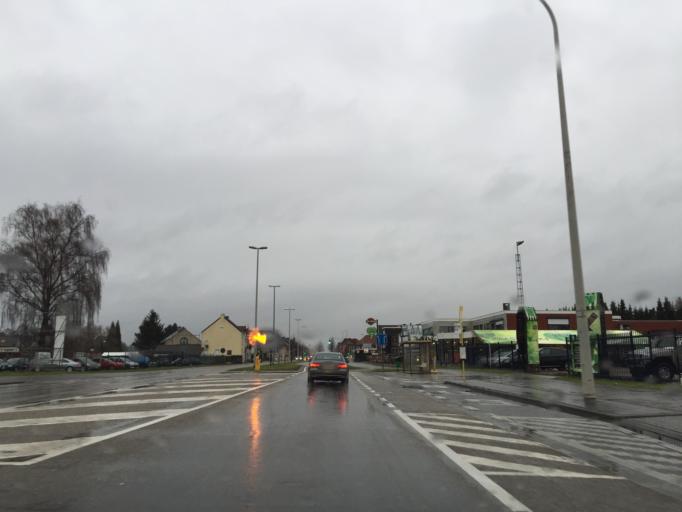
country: BE
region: Flanders
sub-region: Provincie Limburg
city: Lanaken
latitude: 50.9166
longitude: 5.6836
